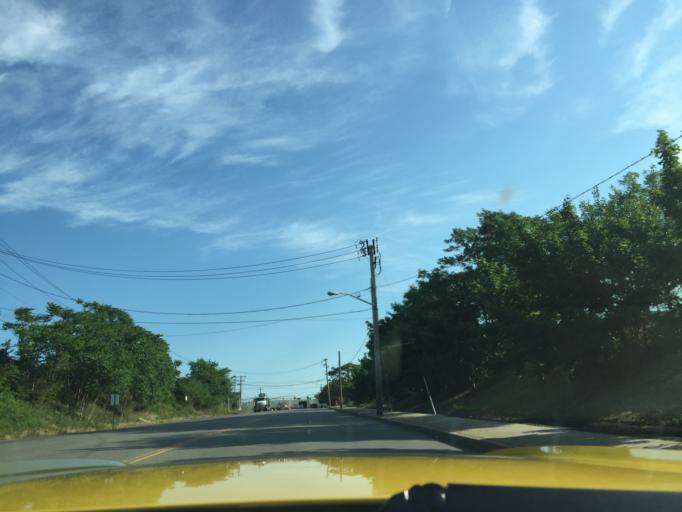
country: US
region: New York
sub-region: Nassau County
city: Salisbury
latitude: 40.7632
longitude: -73.5482
